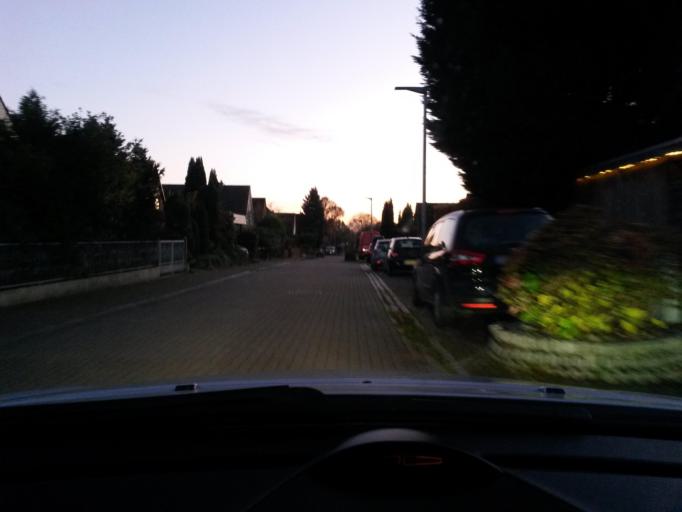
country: DE
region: Schleswig-Holstein
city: Barsbuettel
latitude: 53.5670
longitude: 10.1710
